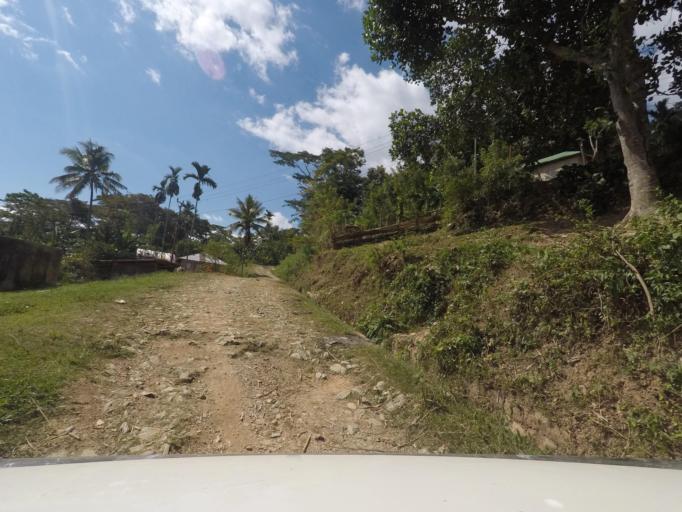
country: TL
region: Ermera
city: Gleno
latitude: -8.7195
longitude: 125.3074
